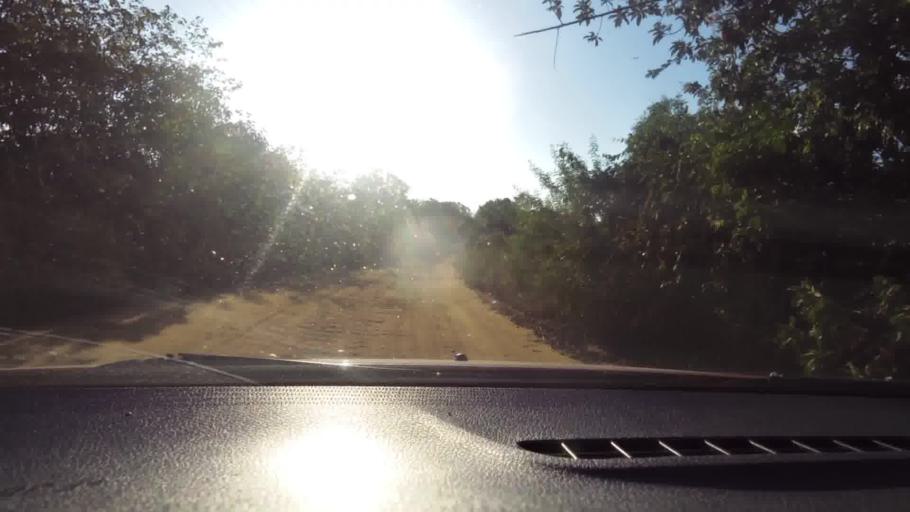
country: BR
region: Espirito Santo
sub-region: Guarapari
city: Guarapari
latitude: -20.5350
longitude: -40.4528
